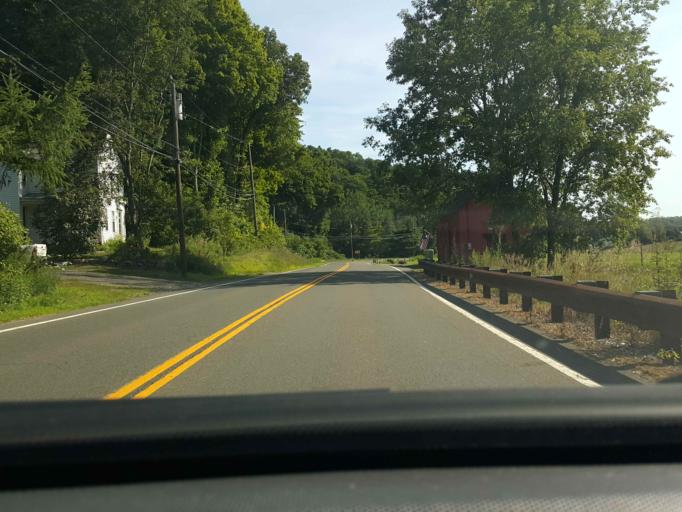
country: US
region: Connecticut
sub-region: New Haven County
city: North Branford
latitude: 41.3760
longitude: -72.7112
